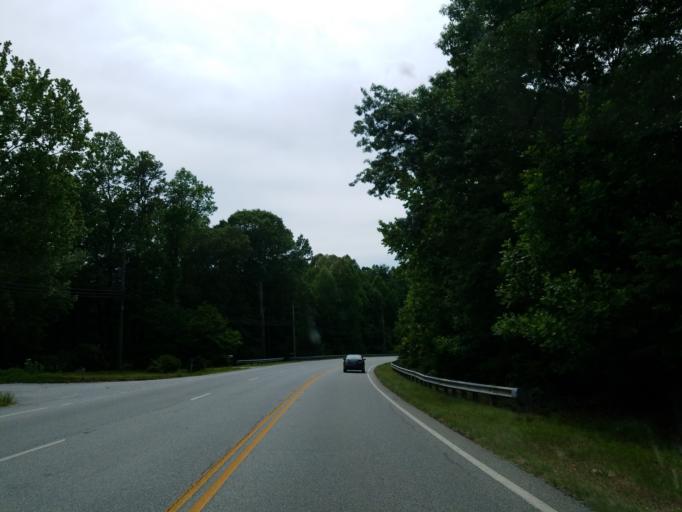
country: US
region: Georgia
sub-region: Lumpkin County
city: Dahlonega
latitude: 34.5421
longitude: -83.9628
